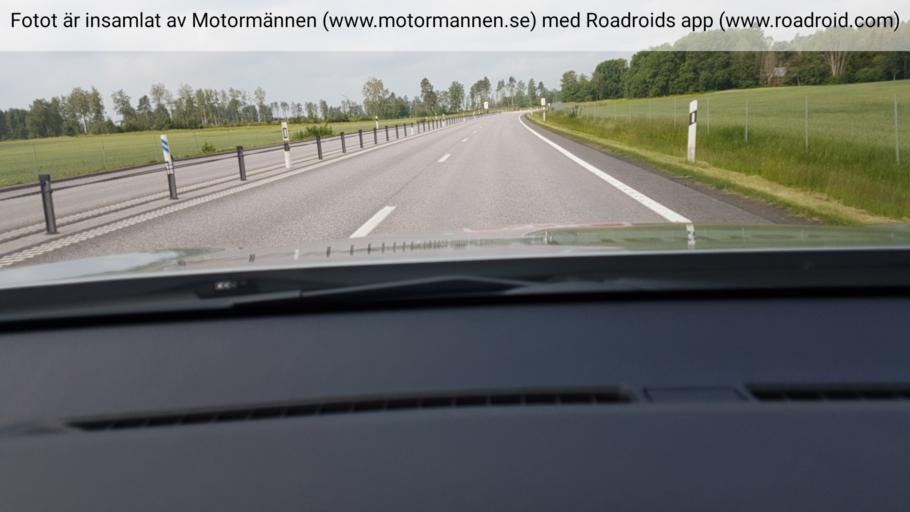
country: SE
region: Vaestra Goetaland
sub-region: Vara Kommun
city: Kvanum
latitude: 58.3454
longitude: 13.2267
